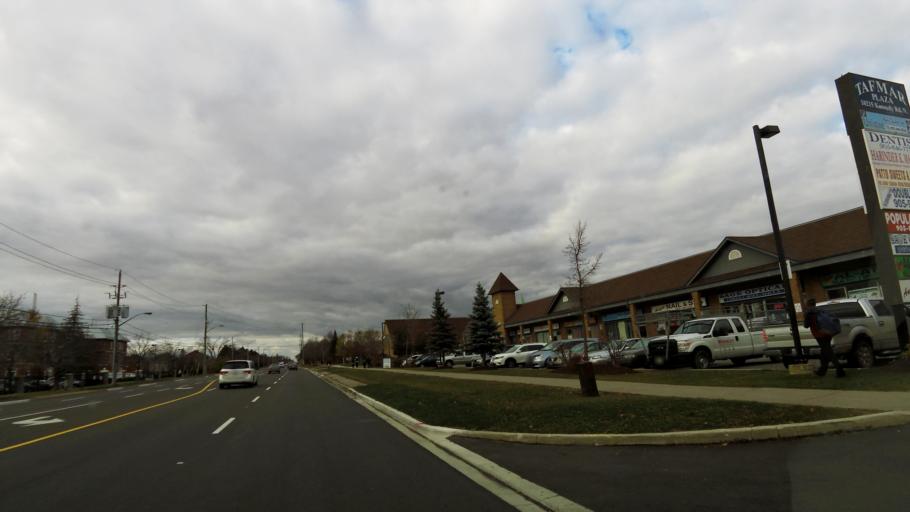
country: CA
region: Ontario
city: Brampton
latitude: 43.7198
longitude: -79.7819
